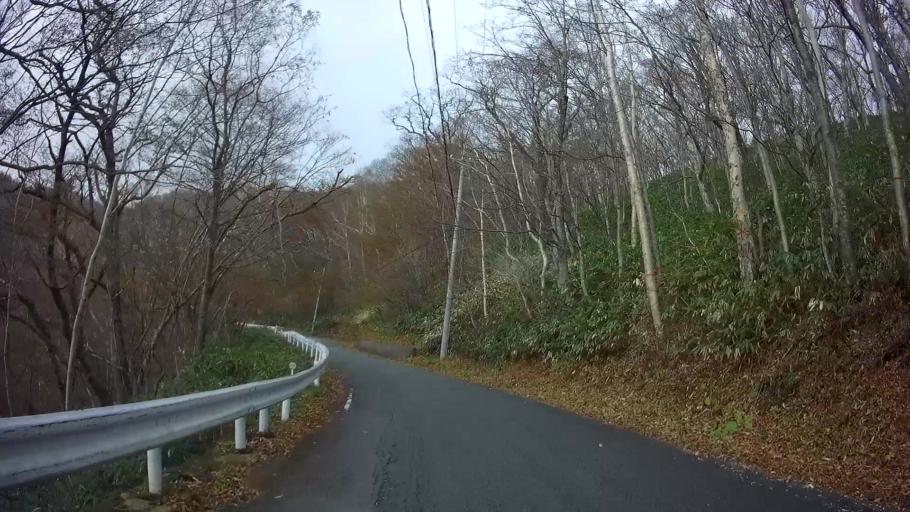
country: JP
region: Gunma
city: Nakanojomachi
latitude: 36.6870
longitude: 138.6550
